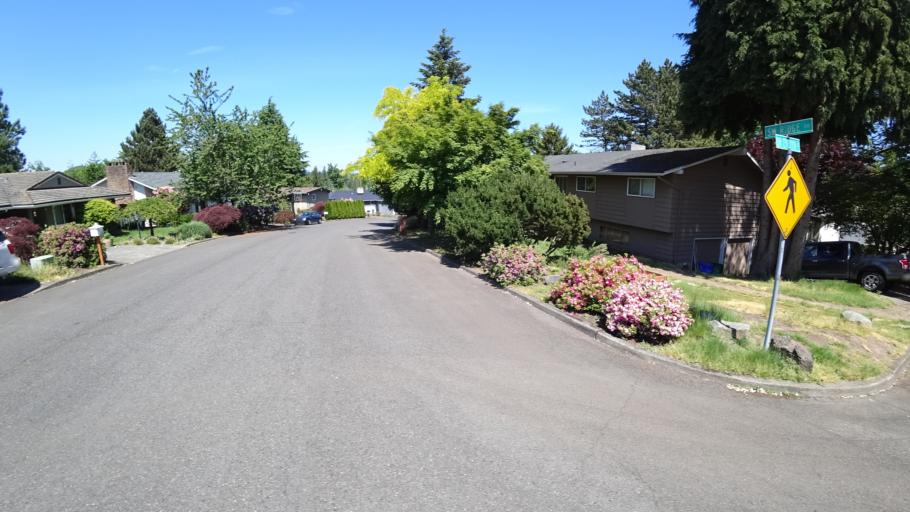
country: US
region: Oregon
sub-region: Washington County
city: Metzger
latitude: 45.4547
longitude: -122.7100
